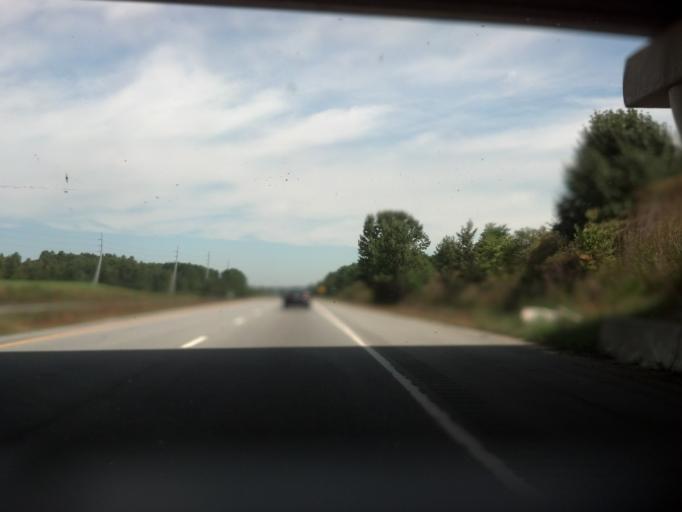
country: US
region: North Carolina
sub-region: Pitt County
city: Summerfield
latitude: 35.6288
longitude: -77.4333
